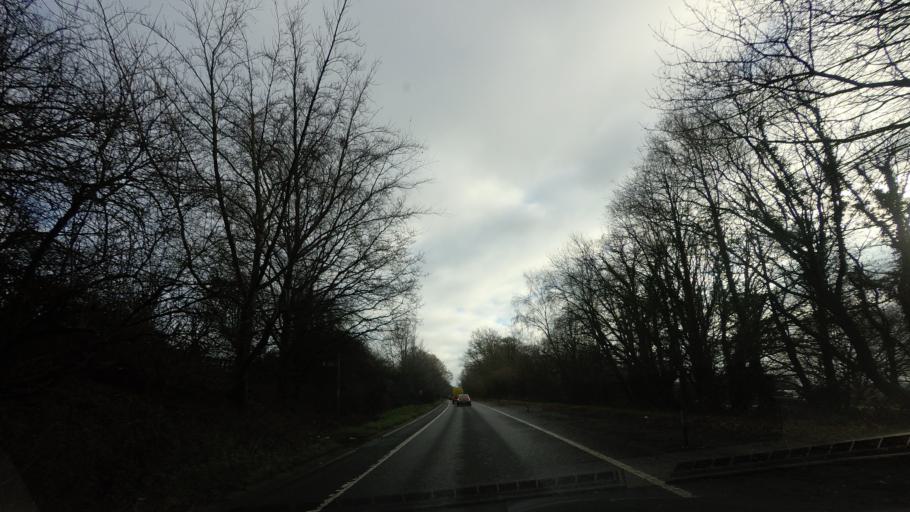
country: GB
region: England
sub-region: Kent
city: Hawkhurst
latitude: 51.0686
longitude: 0.4332
